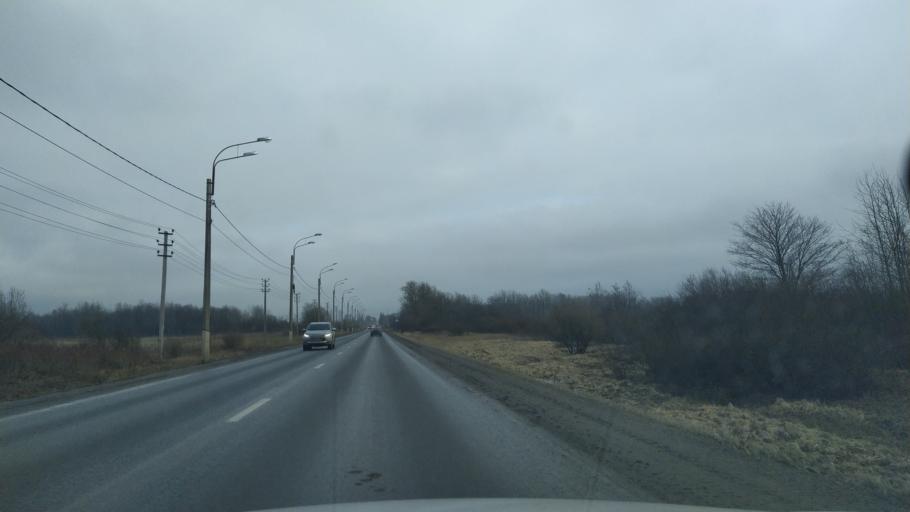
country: RU
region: St.-Petersburg
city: Aleksandrovskaya
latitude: 59.7136
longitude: 30.3039
